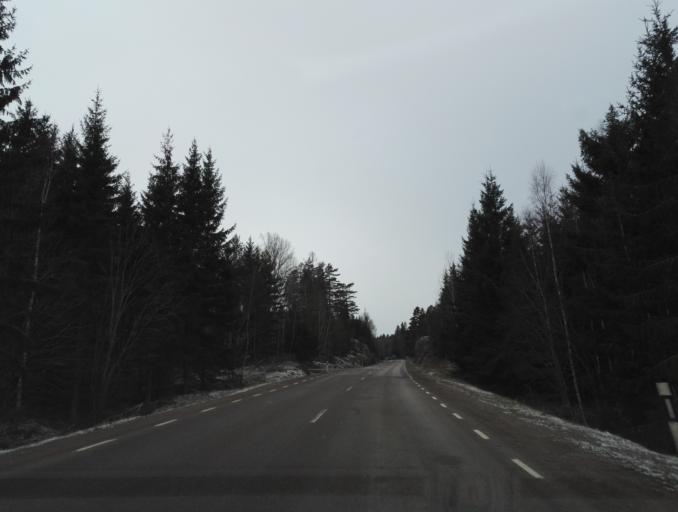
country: SE
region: Kalmar
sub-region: Hultsfreds Kommun
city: Virserum
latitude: 57.3009
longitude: 15.5781
